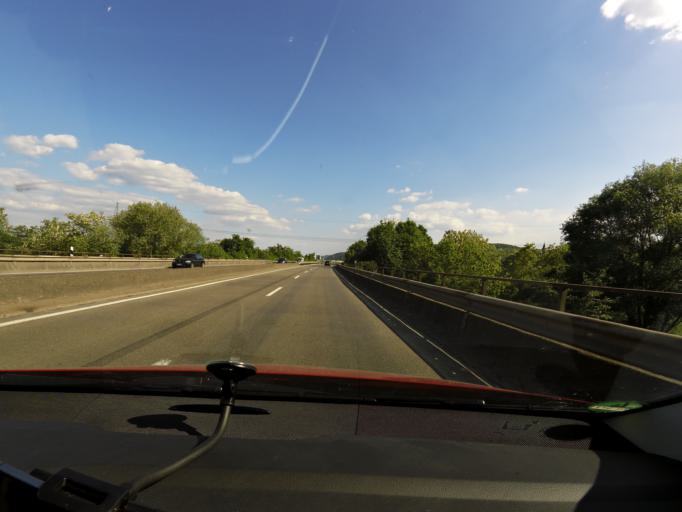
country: DE
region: Rheinland-Pfalz
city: Sinzig
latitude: 50.5525
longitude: 7.2532
